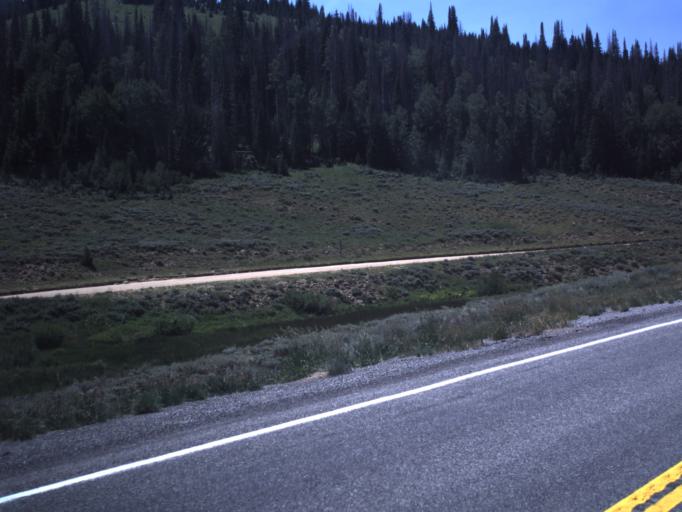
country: US
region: Utah
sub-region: Sanpete County
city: Fairview
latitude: 39.6422
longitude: -111.2439
